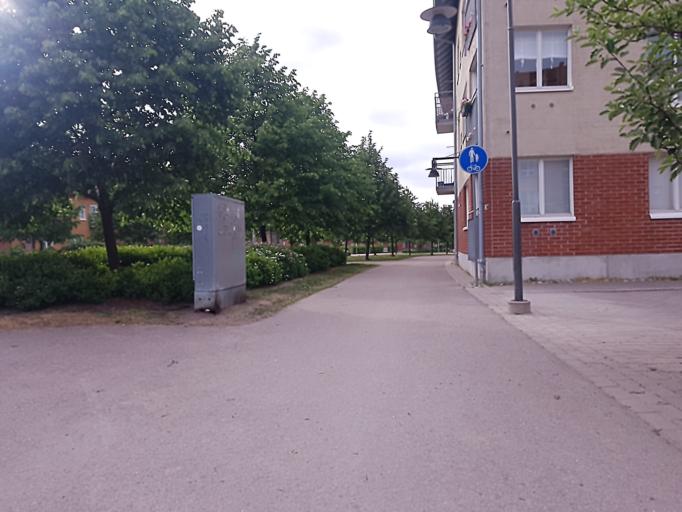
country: FI
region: Uusimaa
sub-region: Helsinki
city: Vantaa
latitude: 60.2818
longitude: 24.9604
